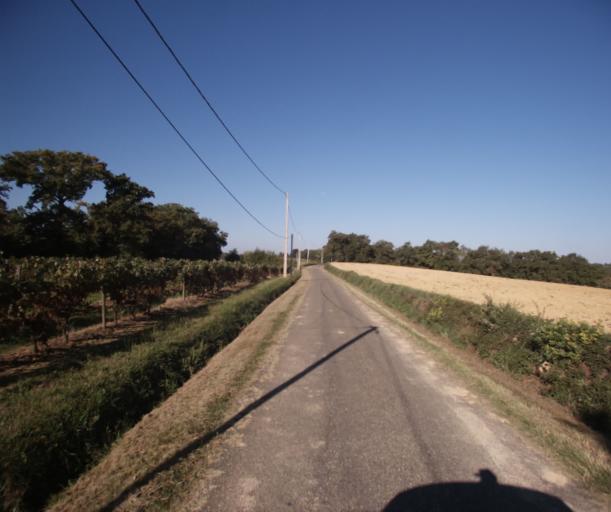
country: FR
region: Midi-Pyrenees
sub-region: Departement du Gers
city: Cazaubon
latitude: 43.9081
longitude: 0.0008
